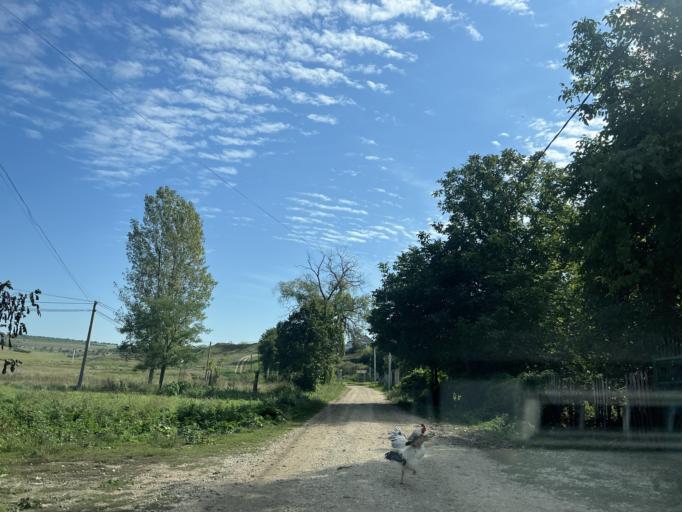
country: MD
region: Ungheni
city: Ungheni
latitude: 47.1960
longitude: 27.8124
